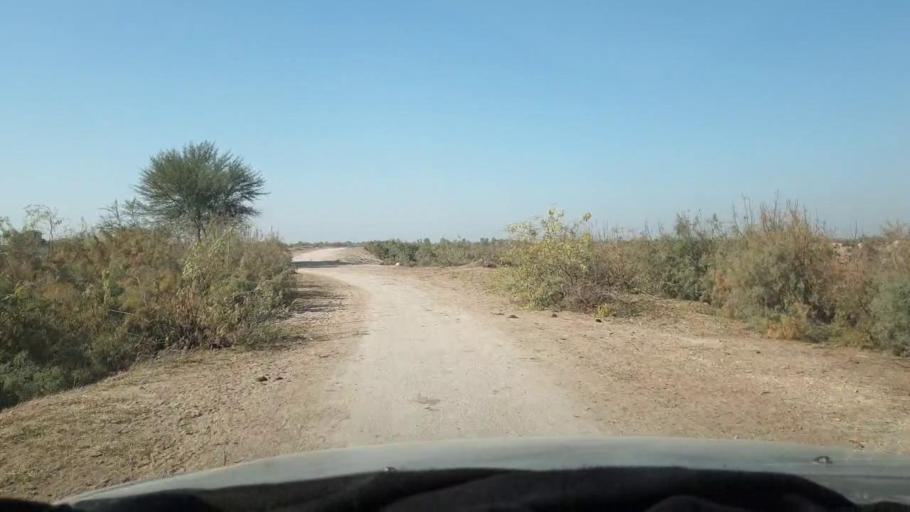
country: PK
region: Sindh
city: Adilpur
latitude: 27.8965
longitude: 69.2478
